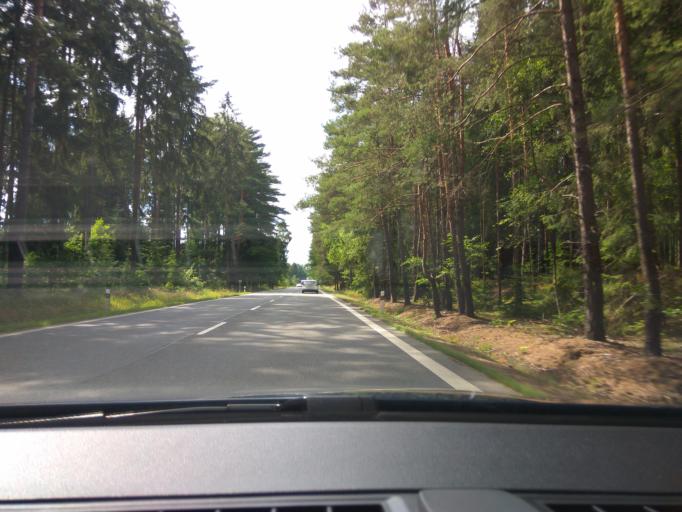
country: CZ
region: Jihocesky
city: Kovarov
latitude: 49.4852
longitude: 14.2588
